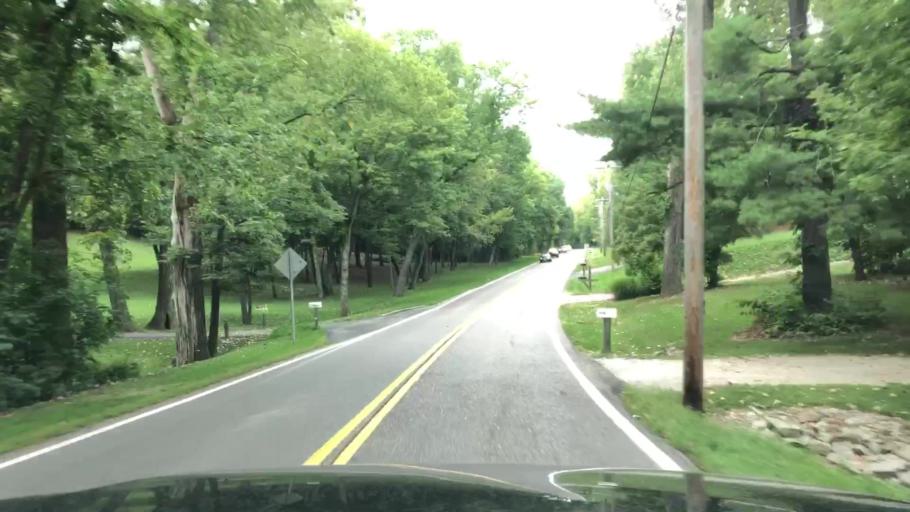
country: US
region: Missouri
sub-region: Saint Louis County
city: Hazelwood
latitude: 38.8087
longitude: -90.3832
